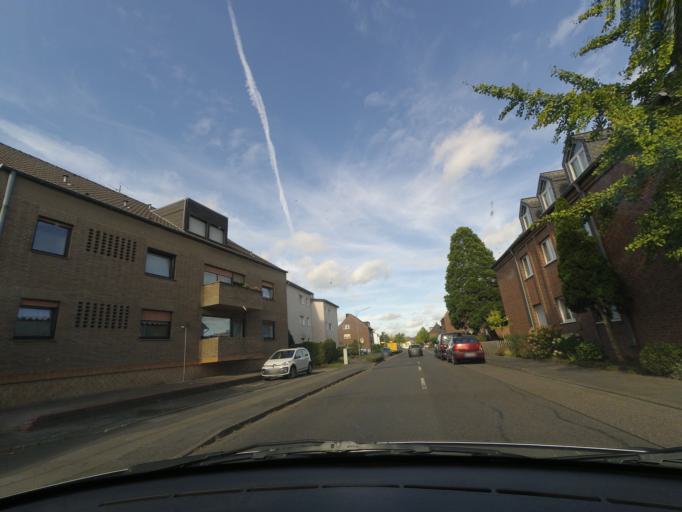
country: DE
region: North Rhine-Westphalia
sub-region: Regierungsbezirk Dusseldorf
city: Korschenbroich
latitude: 51.1905
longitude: 6.5571
